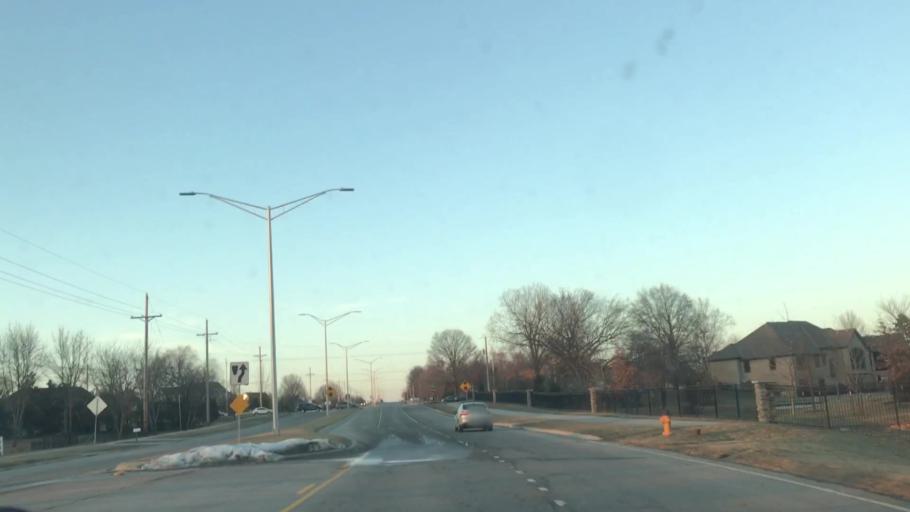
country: US
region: Kansas
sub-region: Johnson County
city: Lenexa
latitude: 38.8383
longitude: -94.7051
